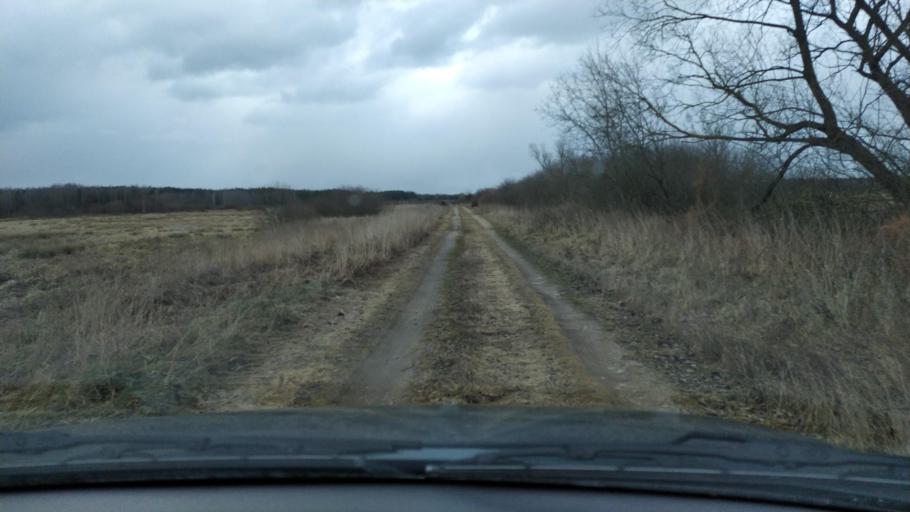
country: BY
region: Brest
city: Zhabinka
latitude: 52.4121
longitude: 24.0648
